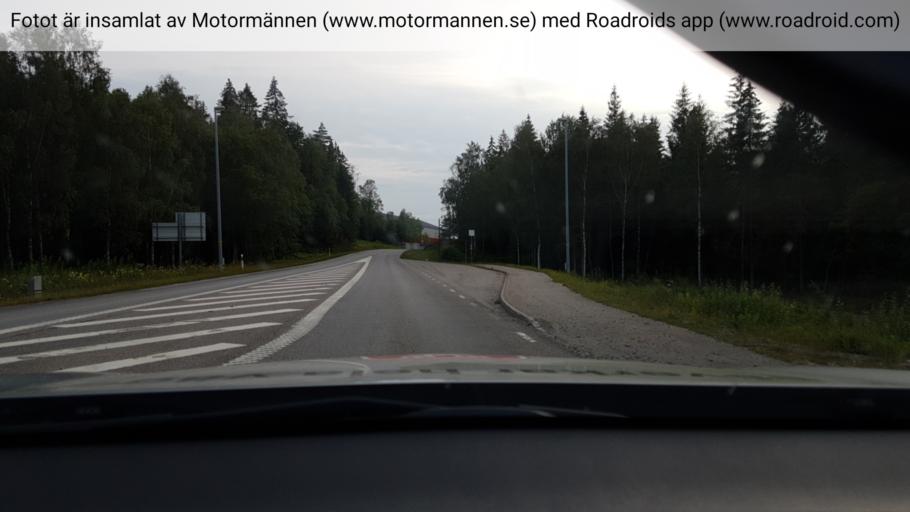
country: SE
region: Vaestra Goetaland
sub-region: Uddevalla Kommun
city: Uddevalla
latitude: 58.3767
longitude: 11.9840
